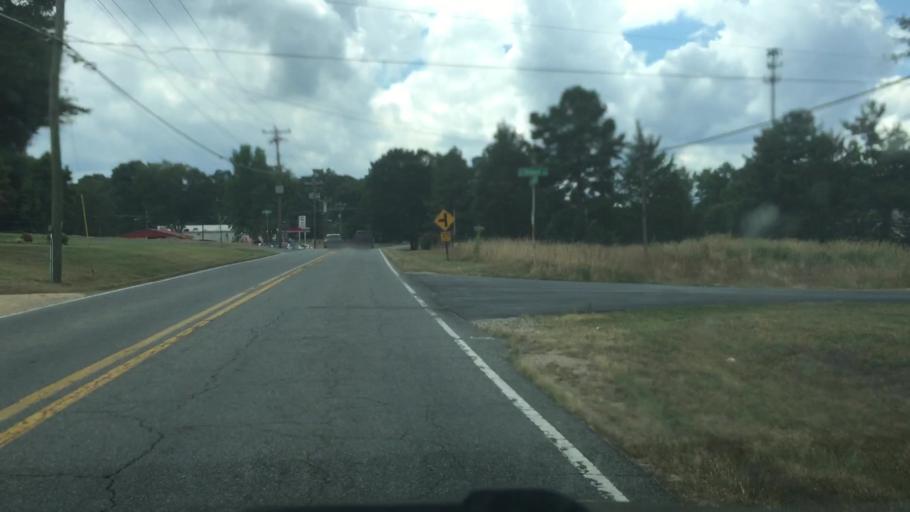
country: US
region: North Carolina
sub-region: Rowan County
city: Enochville
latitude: 35.5184
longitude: -80.6700
